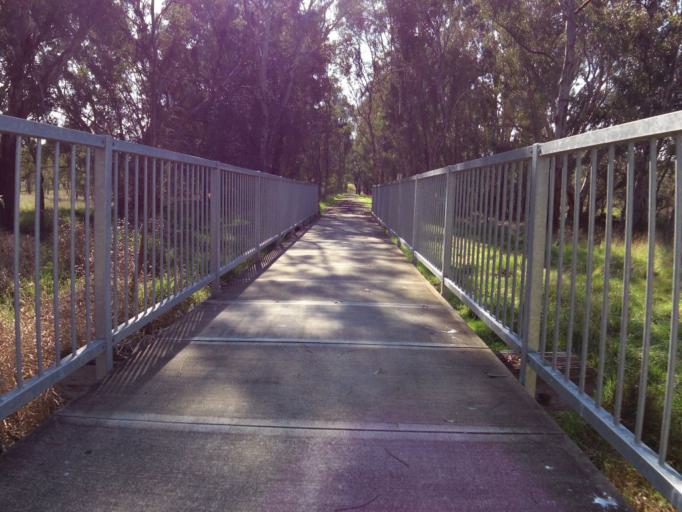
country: AU
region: Victoria
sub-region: Murrindindi
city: Alexandra
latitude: -37.1550
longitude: 145.5749
